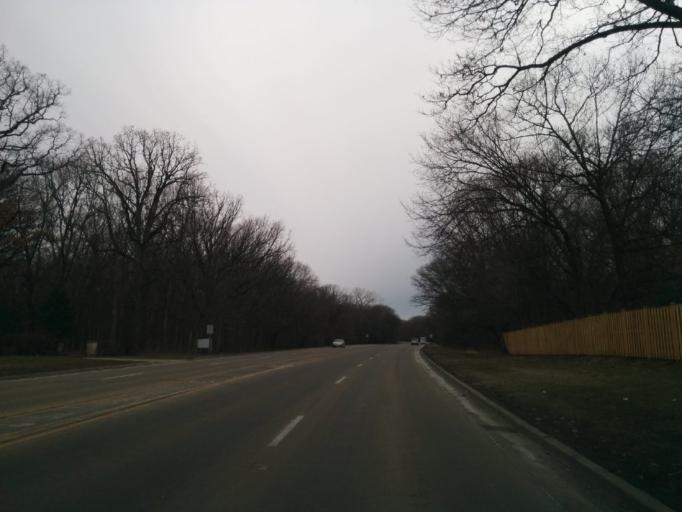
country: US
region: Illinois
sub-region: Cook County
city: Des Plaines
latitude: 42.0868
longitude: -87.8777
